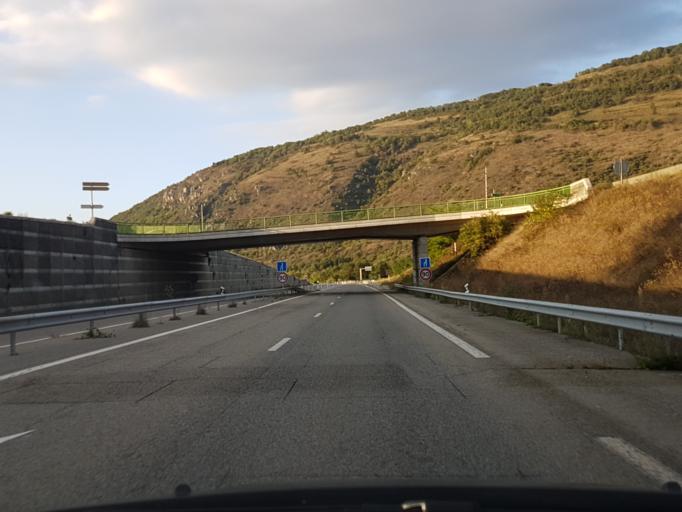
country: FR
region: Midi-Pyrenees
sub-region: Departement de l'Ariege
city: Montgaillard
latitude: 42.9506
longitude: 1.6228
